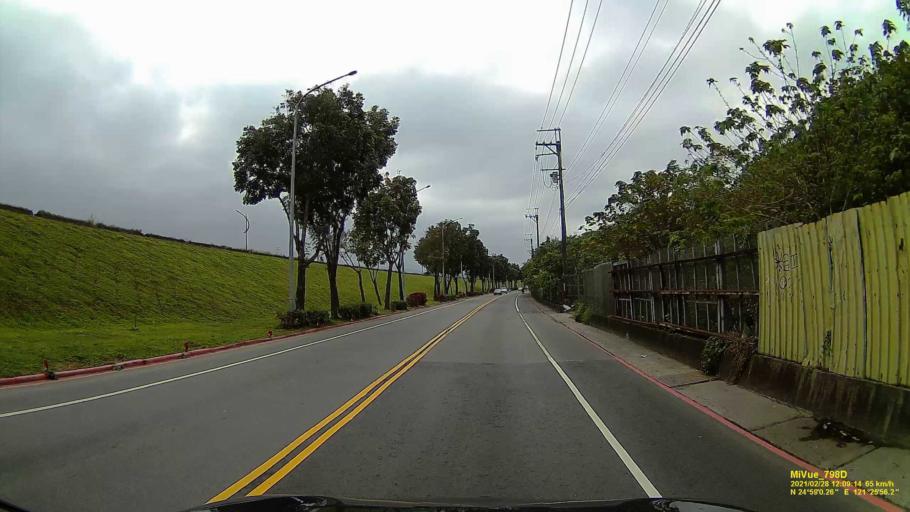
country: TW
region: Taipei
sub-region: Taipei
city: Banqiao
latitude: 24.9832
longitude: 121.4321
